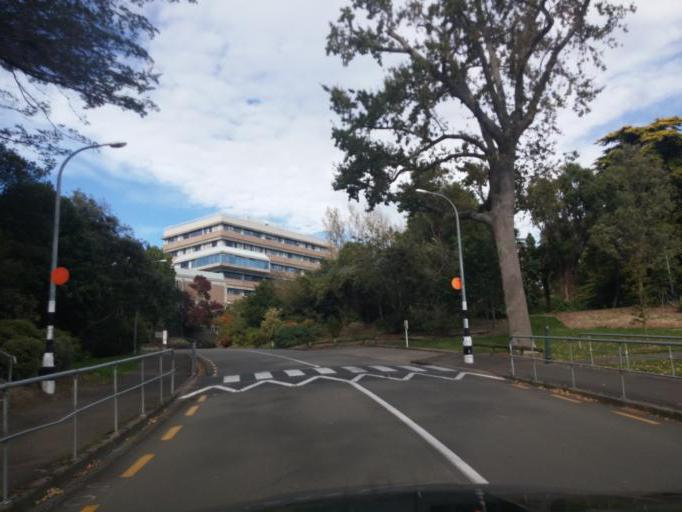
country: NZ
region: Manawatu-Wanganui
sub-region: Palmerston North City
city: Palmerston North
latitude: -40.3836
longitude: 175.6164
